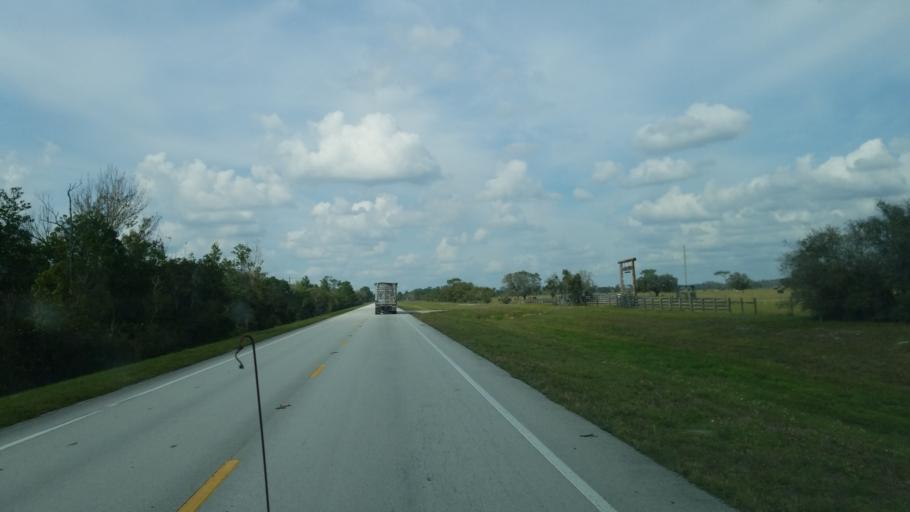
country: US
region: Florida
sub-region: Indian River County
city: Fellsmere
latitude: 27.7094
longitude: -80.9093
